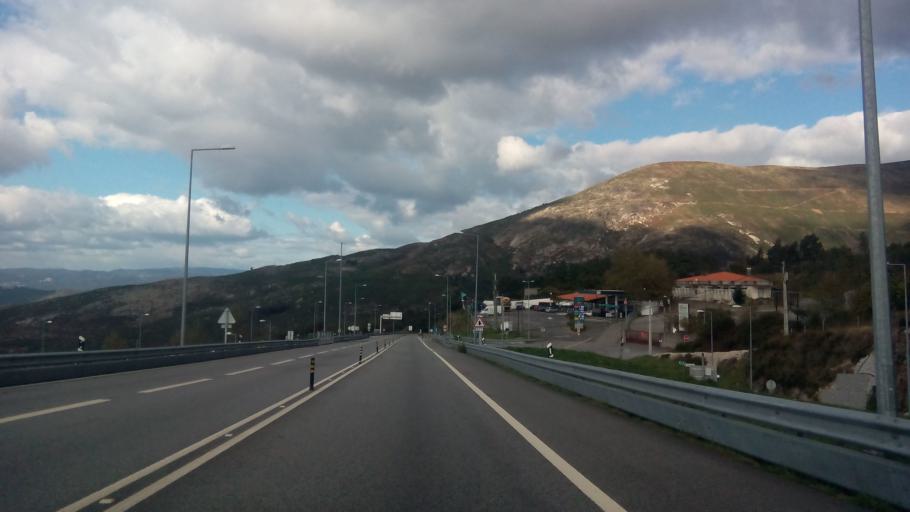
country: PT
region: Porto
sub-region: Baiao
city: Valadares
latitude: 41.2587
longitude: -7.9696
